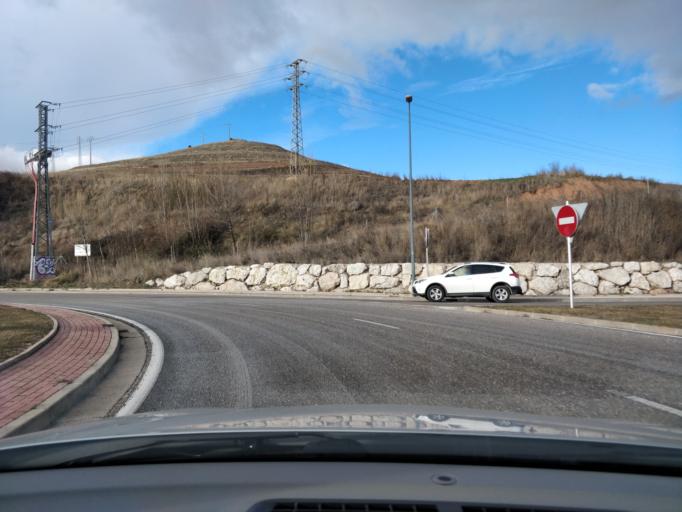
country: ES
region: Castille and Leon
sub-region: Provincia de Burgos
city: Villagonzalo-Pedernales
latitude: 42.3472
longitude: -3.7233
